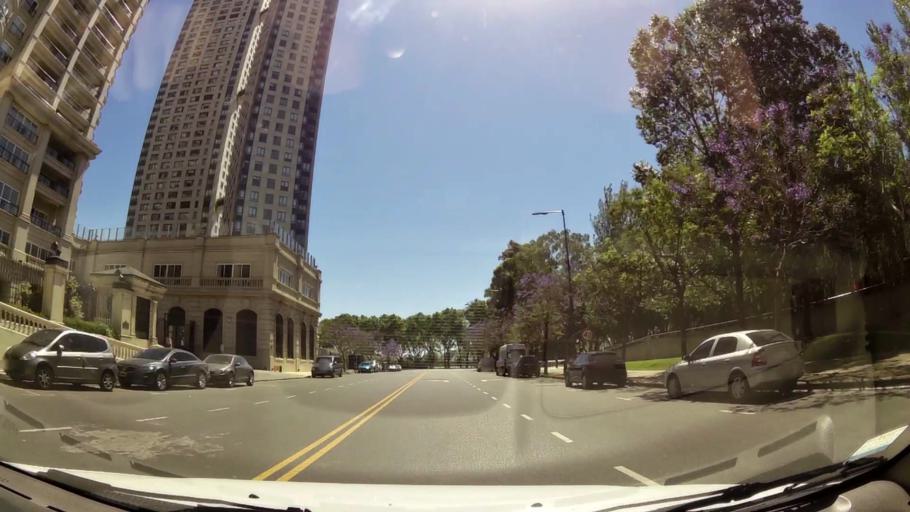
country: AR
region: Buenos Aires F.D.
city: Buenos Aires
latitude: -34.6133
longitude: -58.3598
